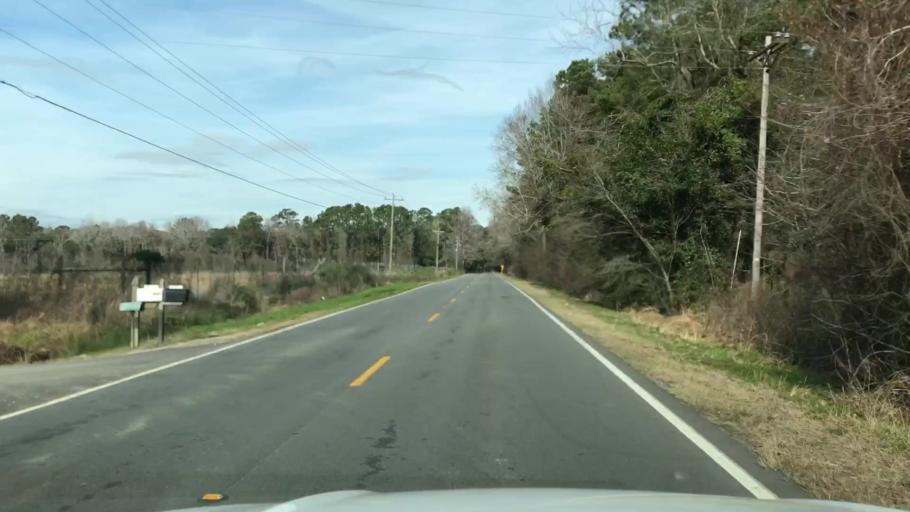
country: US
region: South Carolina
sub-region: Charleston County
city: Folly Beach
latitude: 32.7221
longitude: -80.0226
